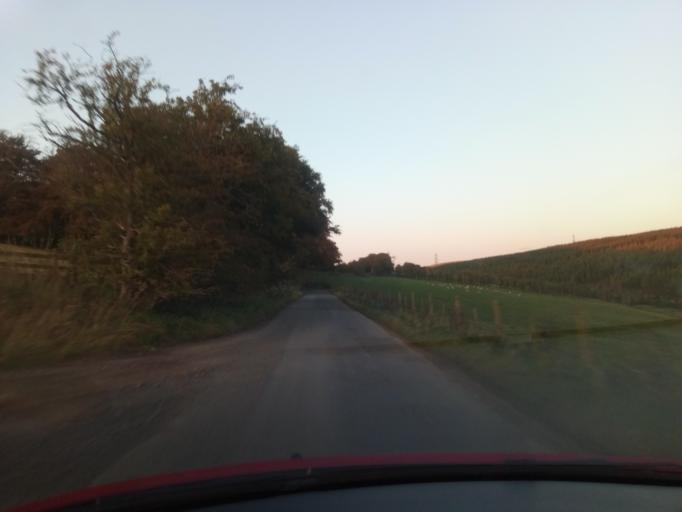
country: GB
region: Scotland
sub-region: Fife
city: Pathhead
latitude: 55.7892
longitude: -2.8938
